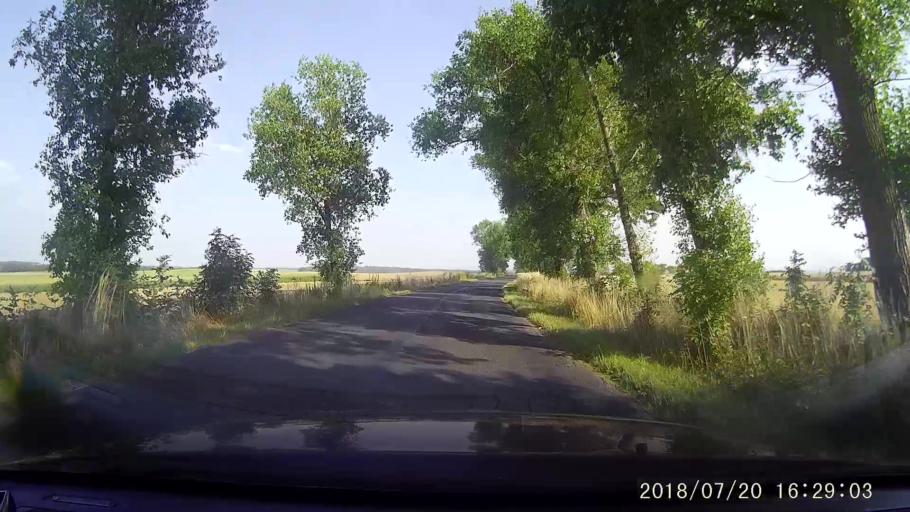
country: PL
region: Lower Silesian Voivodeship
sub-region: Powiat zgorzelecki
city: Sulikow
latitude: 51.1151
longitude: 15.0634
